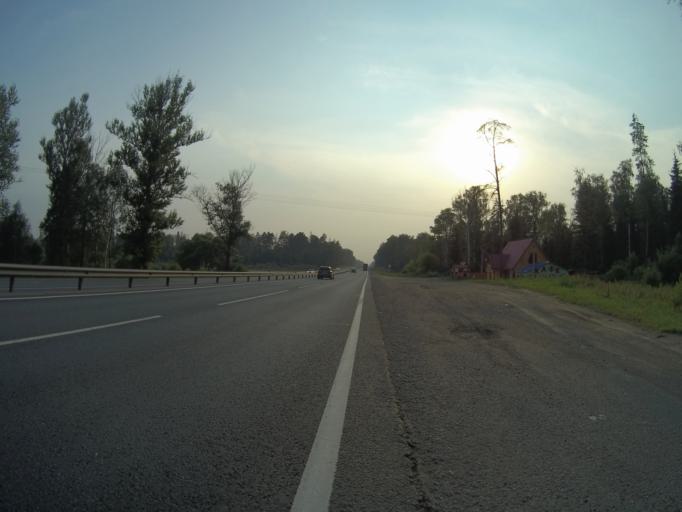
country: RU
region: Vladimir
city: Novki
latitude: 56.2013
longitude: 41.0924
